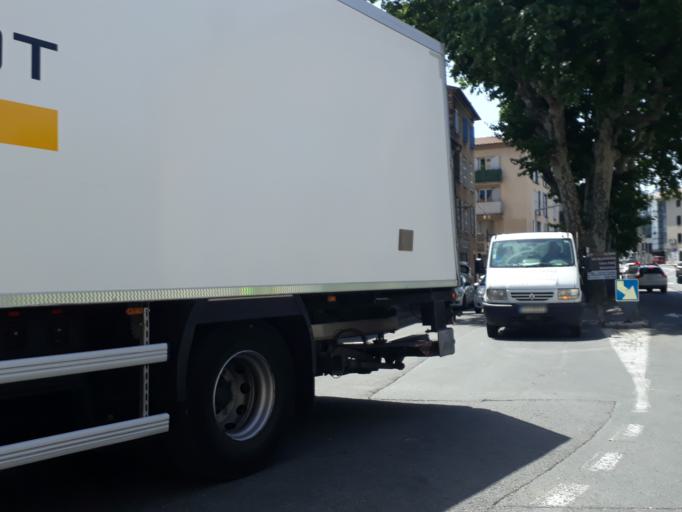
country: FR
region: Provence-Alpes-Cote d'Azur
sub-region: Departement du Var
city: Brignoles
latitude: 43.4080
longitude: 6.0640
